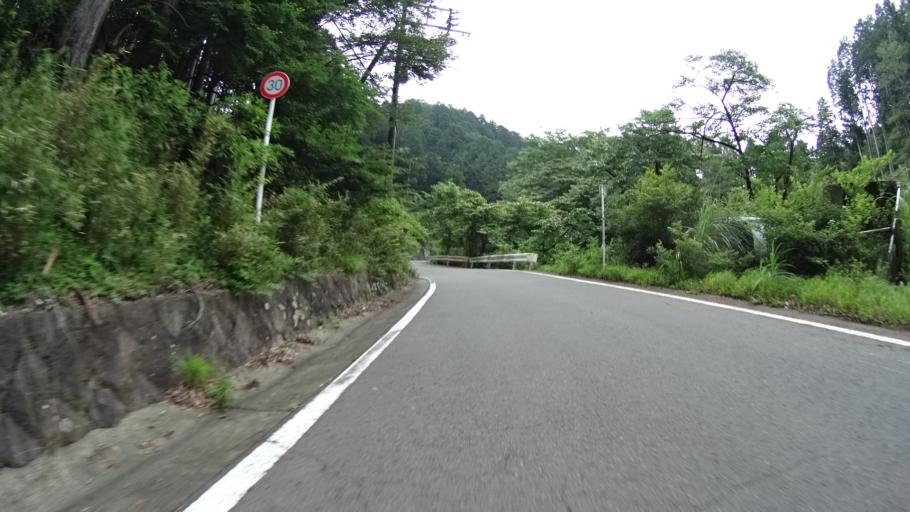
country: JP
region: Kanagawa
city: Hadano
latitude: 35.4376
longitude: 139.2114
